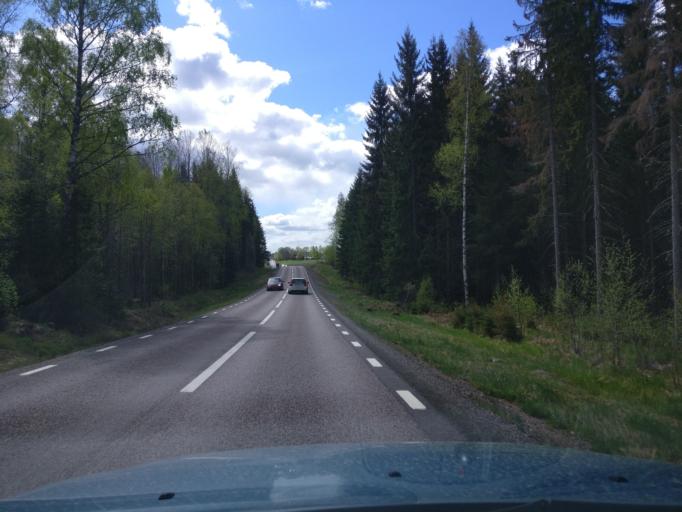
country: SE
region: Vaermland
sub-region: Karlstads Kommun
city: Molkom
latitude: 59.7250
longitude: 13.6787
